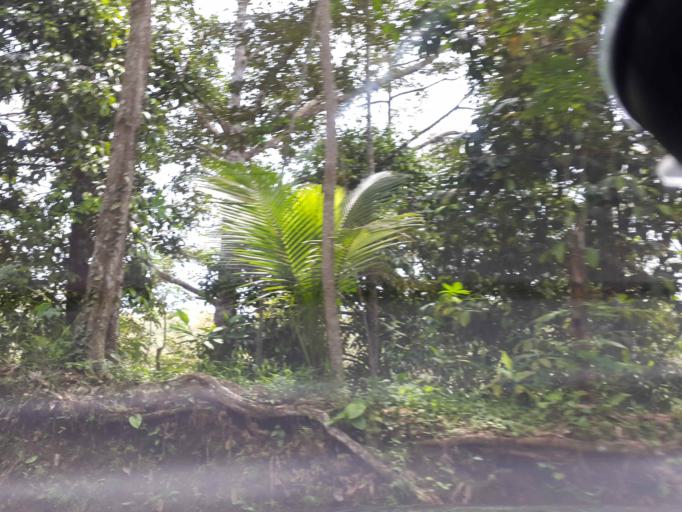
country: ID
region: Central Java
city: Kutoarjo
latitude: -7.7625
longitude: 110.0710
